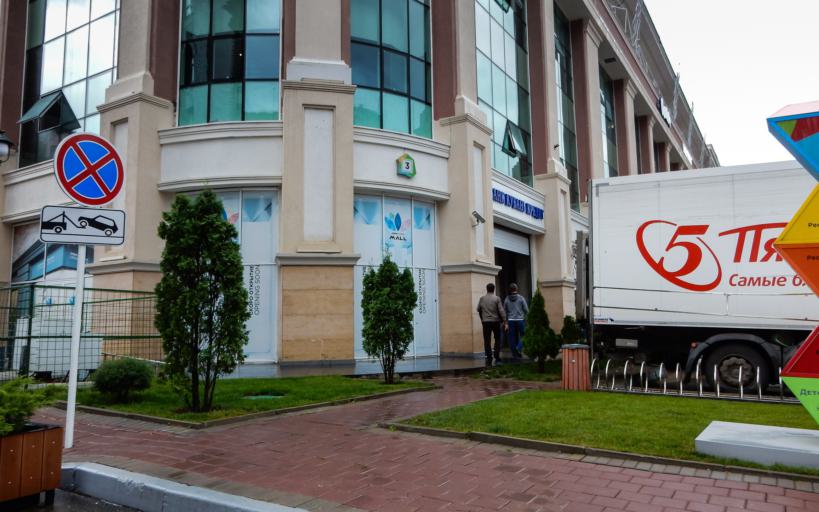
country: RU
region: Krasnodarskiy
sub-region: Sochi City
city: Krasnaya Polyana
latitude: 43.6842
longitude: 40.2638
